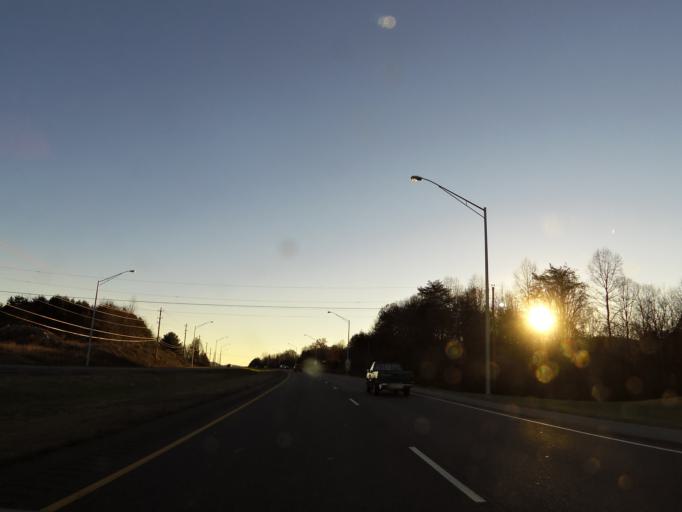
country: US
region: Tennessee
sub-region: Anderson County
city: Clinton
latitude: 36.1383
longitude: -84.1069
